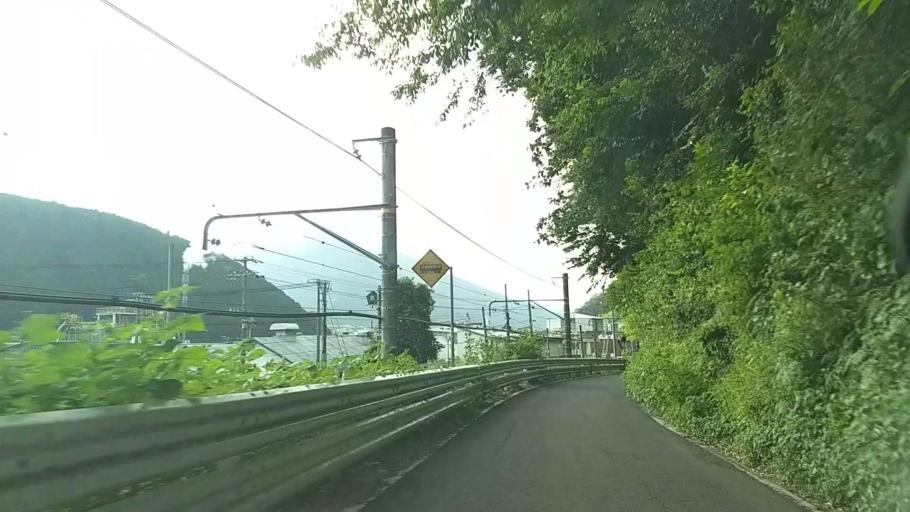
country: JP
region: Shizuoka
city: Fujinomiya
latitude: 35.1955
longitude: 138.5653
